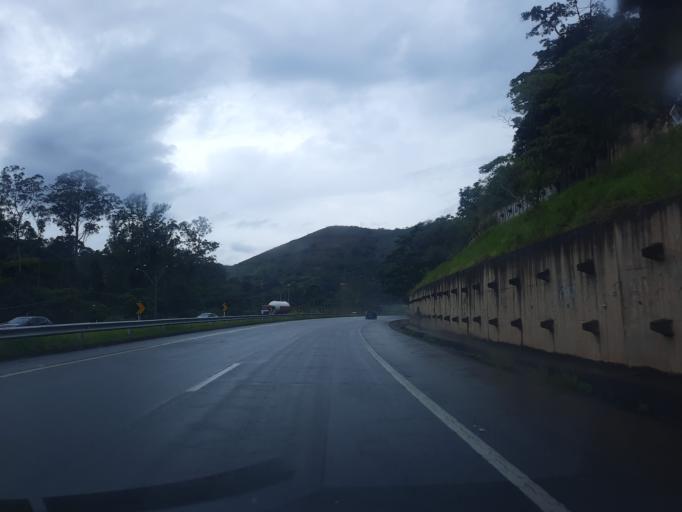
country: BR
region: Rio de Janeiro
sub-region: Petropolis
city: Petropolis
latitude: -22.4280
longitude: -43.1645
